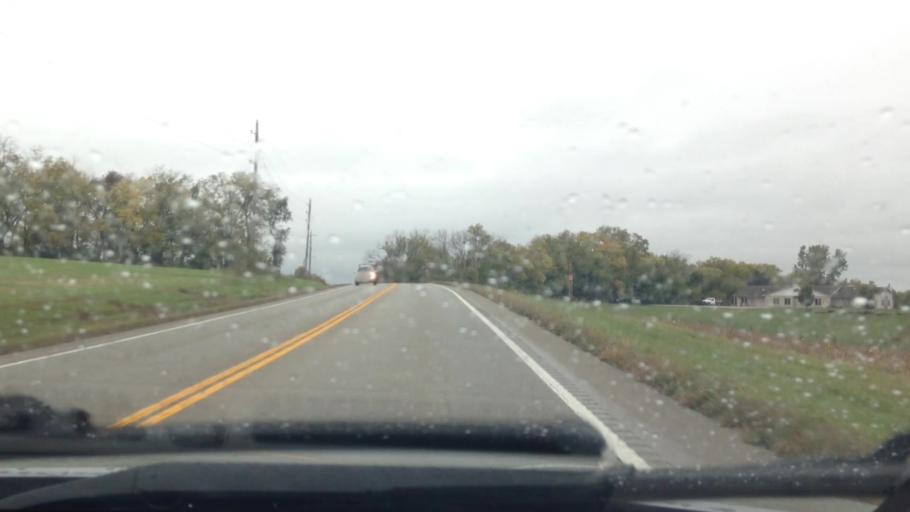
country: US
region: Missouri
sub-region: Platte County
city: Weston
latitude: 39.4065
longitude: -94.8668
